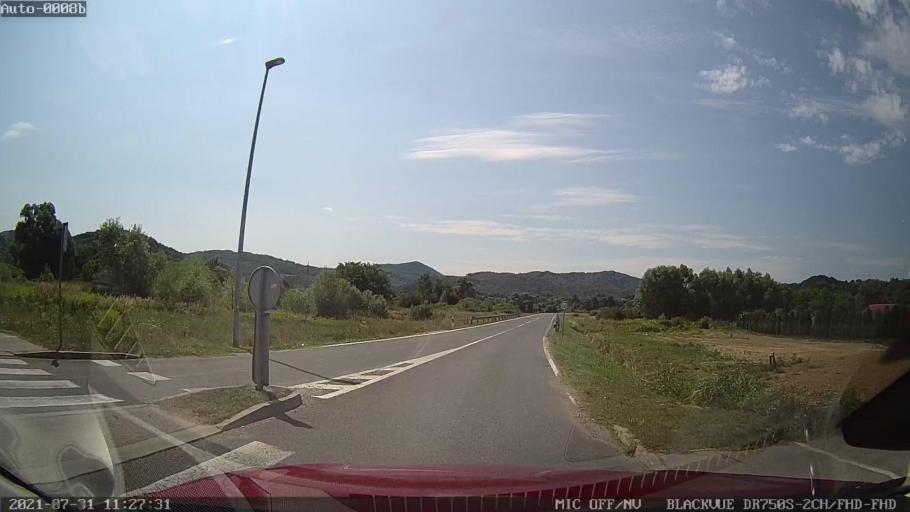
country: HR
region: Varazdinska
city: Ljubescica
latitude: 46.2081
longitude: 16.4316
